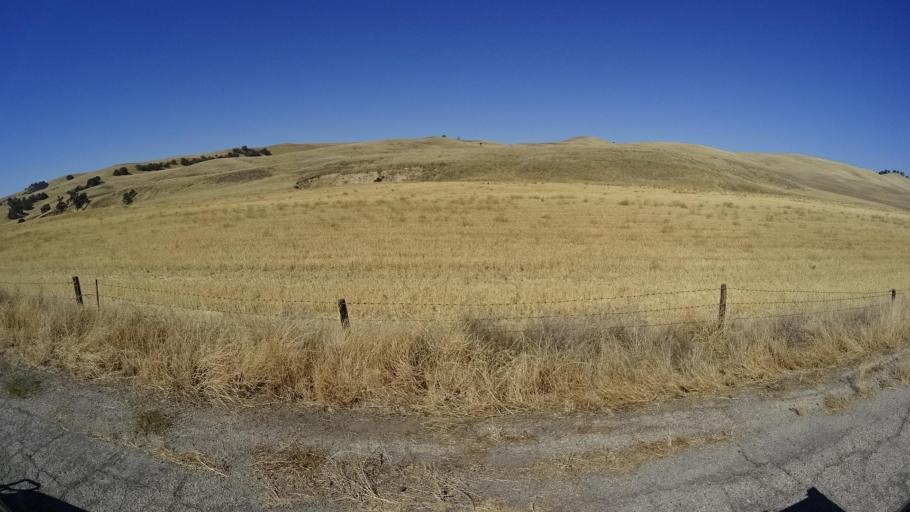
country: US
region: California
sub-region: San Luis Obispo County
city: San Miguel
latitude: 35.7879
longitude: -120.5415
